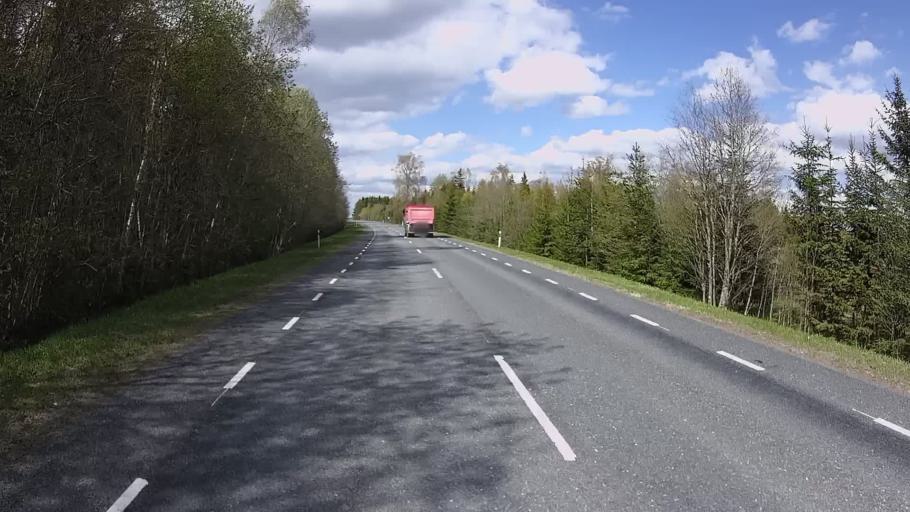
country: EE
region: Jaervamaa
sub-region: Jaerva-Jaani vald
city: Jarva-Jaani
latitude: 59.1028
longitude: 25.8134
